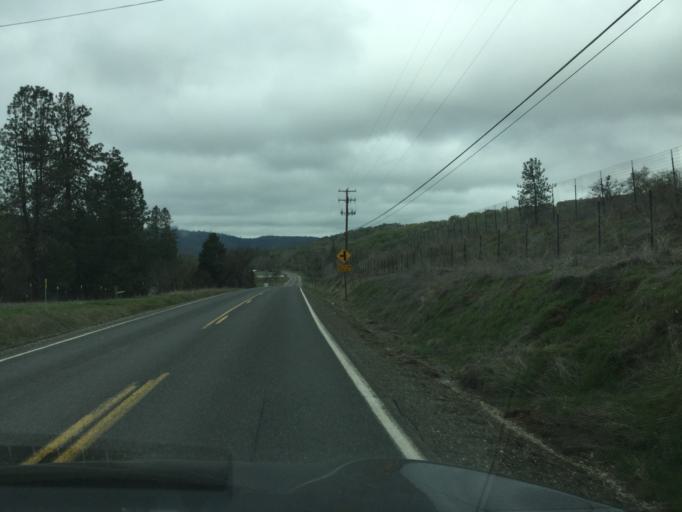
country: US
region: Oregon
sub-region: Jackson County
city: Gold Hill
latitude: 42.3927
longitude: -122.9940
